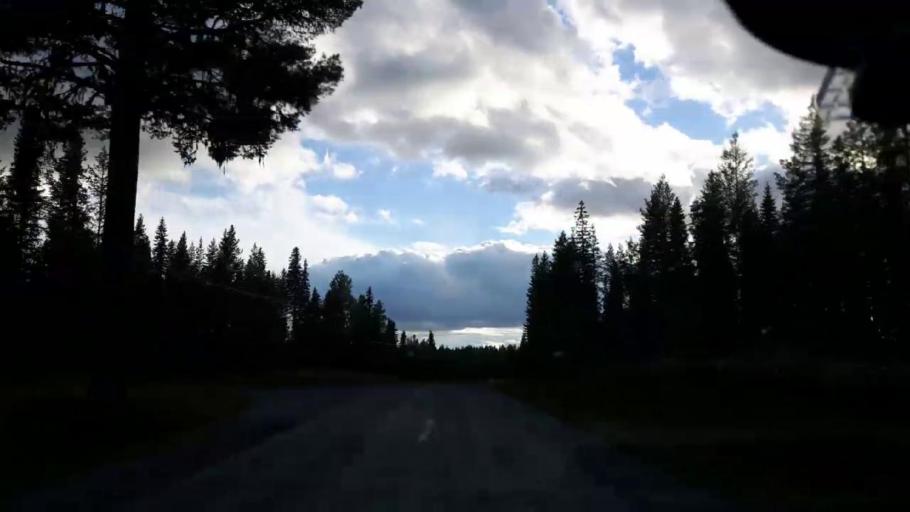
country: SE
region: Jaemtland
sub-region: Stroemsunds Kommun
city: Stroemsund
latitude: 63.3348
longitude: 15.5727
